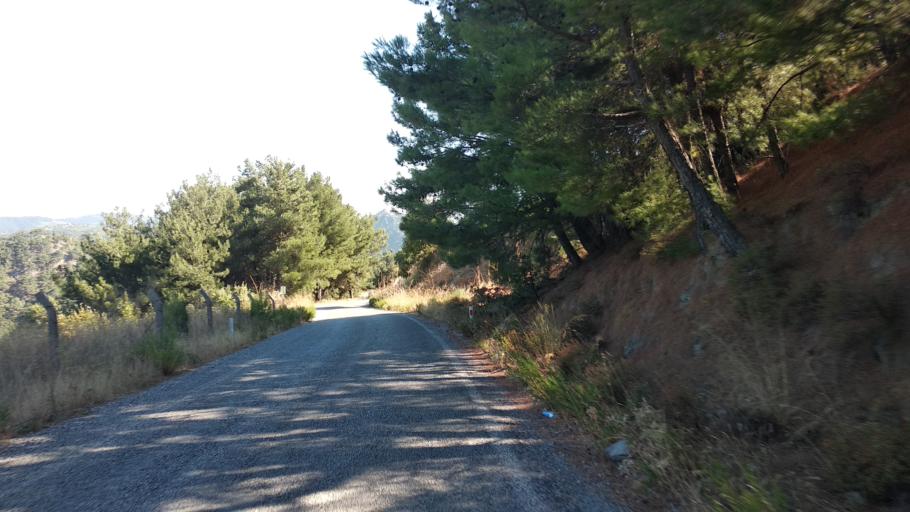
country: TR
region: Izmir
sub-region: Seferihisar
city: Seferhisar
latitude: 38.3281
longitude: 26.9423
